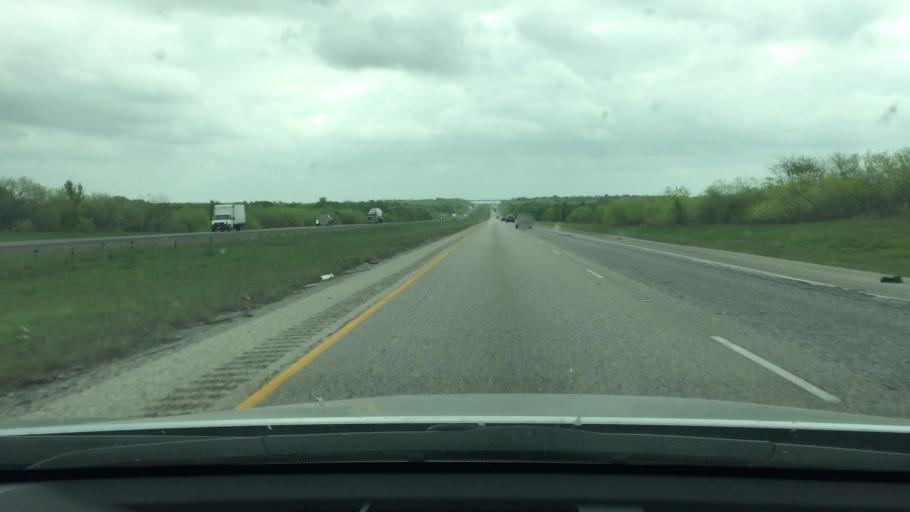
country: US
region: Texas
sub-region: Gonzales County
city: Waelder
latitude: 29.6649
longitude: -97.3534
